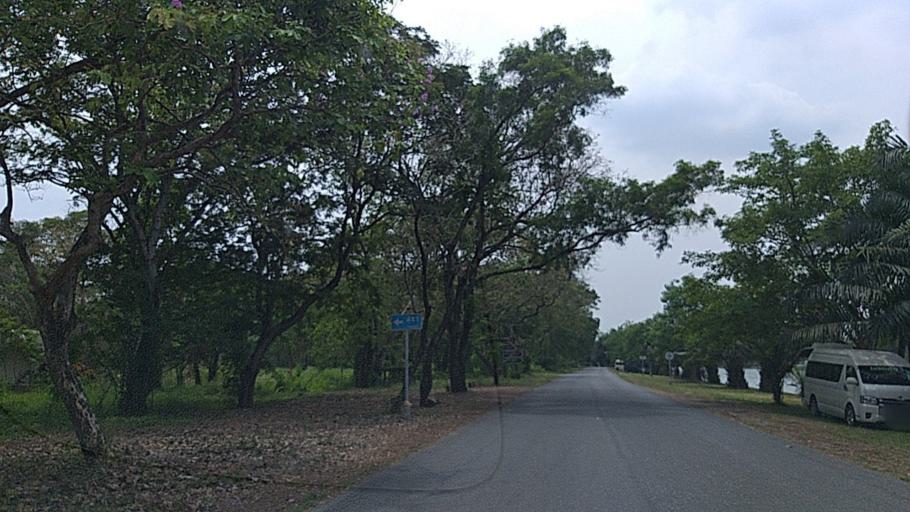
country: TH
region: Bangkok
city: Thawi Watthana
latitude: 13.7788
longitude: 100.3108
